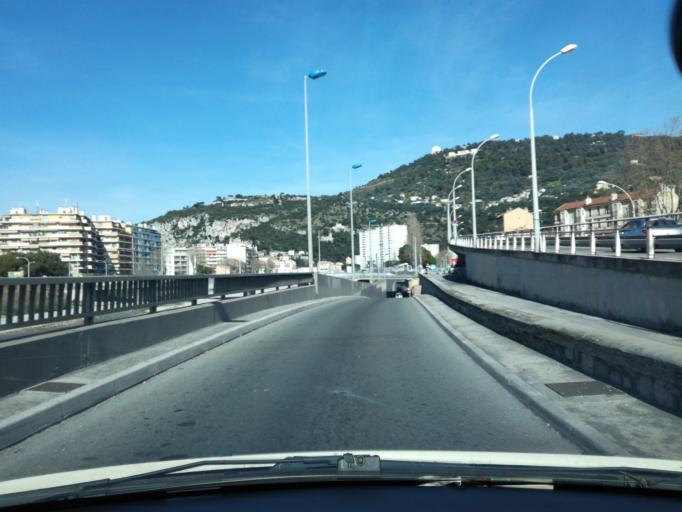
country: FR
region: Provence-Alpes-Cote d'Azur
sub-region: Departement des Alpes-Maritimes
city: Saint-Andre-de-la-Roche
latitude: 43.7178
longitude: 7.2833
